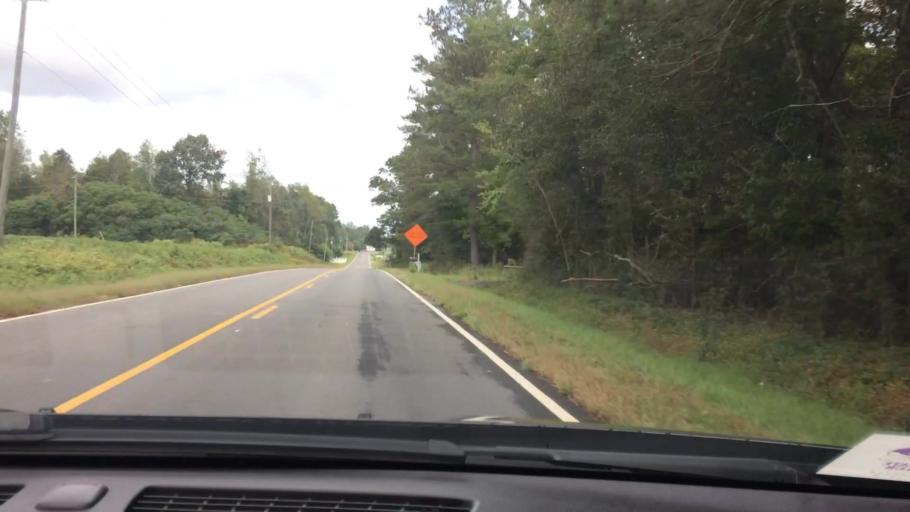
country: US
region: North Carolina
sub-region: Pitt County
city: Ayden
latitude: 35.4600
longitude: -77.4678
